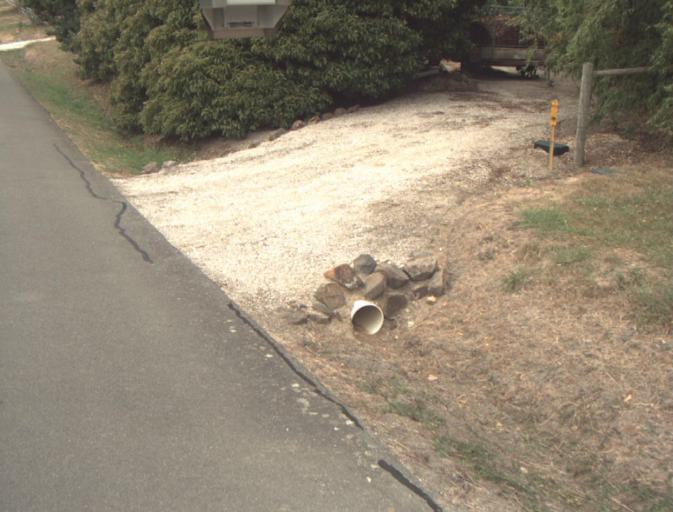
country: AU
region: Tasmania
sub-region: Launceston
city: Mayfield
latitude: -41.3280
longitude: 147.0661
